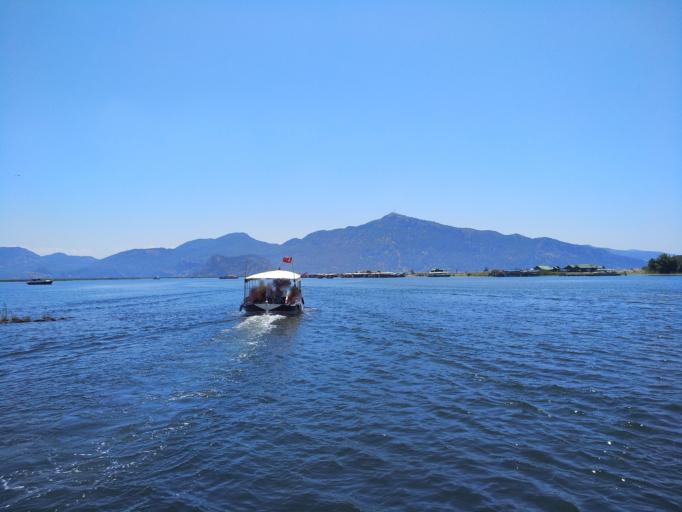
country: TR
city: Dalyan
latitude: 36.8040
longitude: 28.6049
